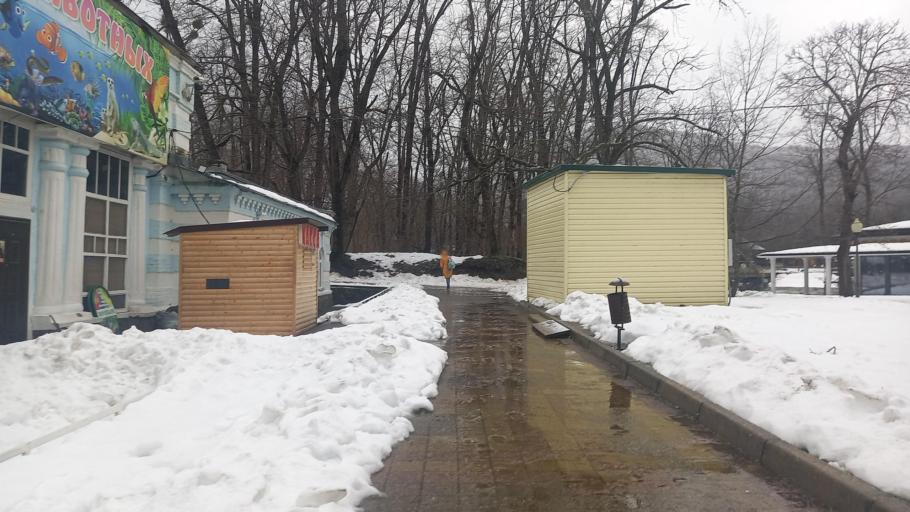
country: RU
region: Krasnodarskiy
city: Goryachiy Klyuch
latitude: 44.6233
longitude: 39.0935
